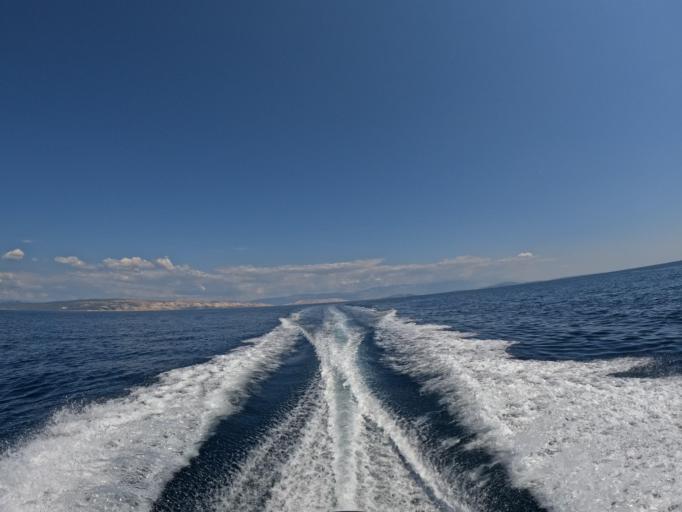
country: HR
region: Primorsko-Goranska
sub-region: Grad Krk
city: Krk
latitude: 44.9290
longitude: 14.5281
